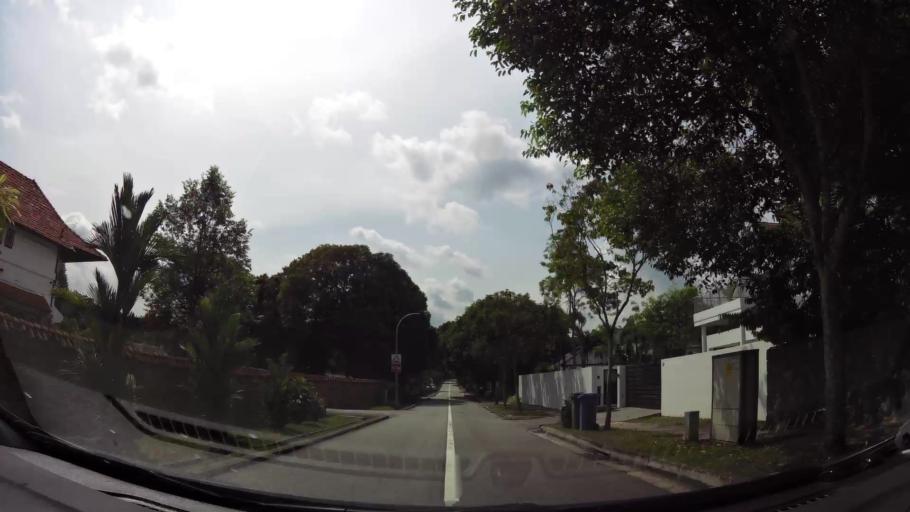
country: SG
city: Singapore
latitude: 1.3395
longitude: 103.7899
